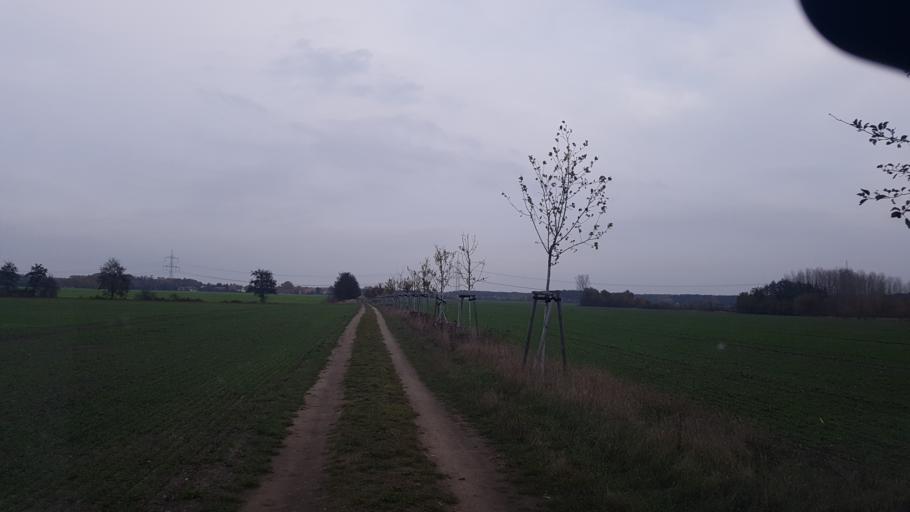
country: DE
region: Brandenburg
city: Schilda
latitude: 51.6304
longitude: 13.3575
